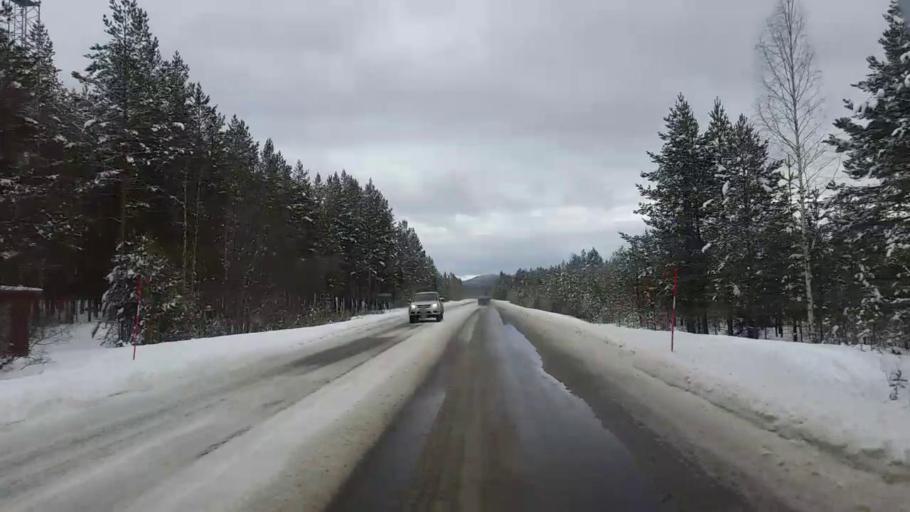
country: SE
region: Vaesternorrland
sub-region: Ange Kommun
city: Ange
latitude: 62.0409
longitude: 15.1876
